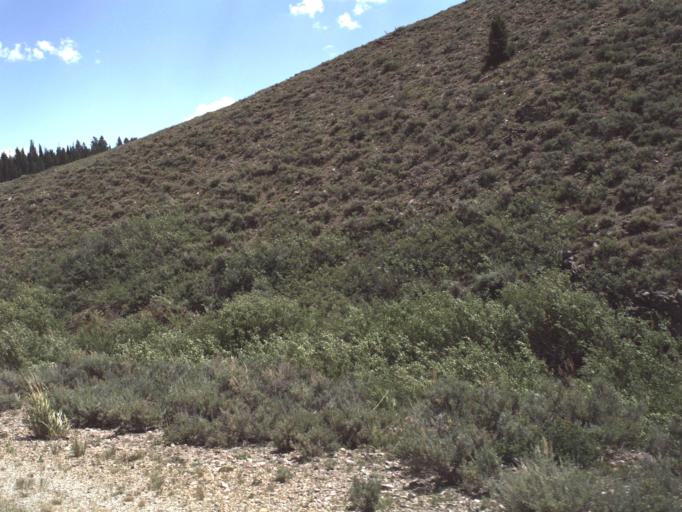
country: US
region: Utah
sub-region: Rich County
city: Randolph
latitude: 41.4846
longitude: -111.3961
